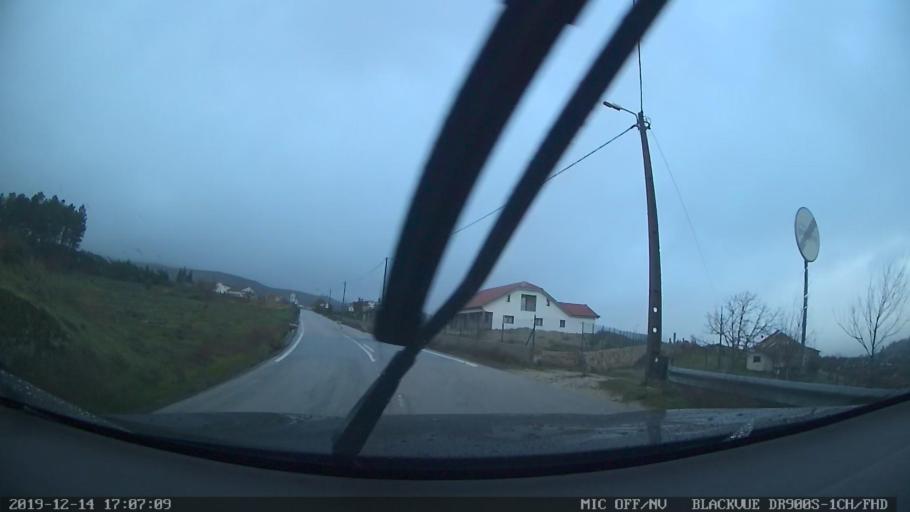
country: PT
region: Vila Real
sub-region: Vila Pouca de Aguiar
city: Vila Pouca de Aguiar
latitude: 41.4599
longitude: -7.5965
